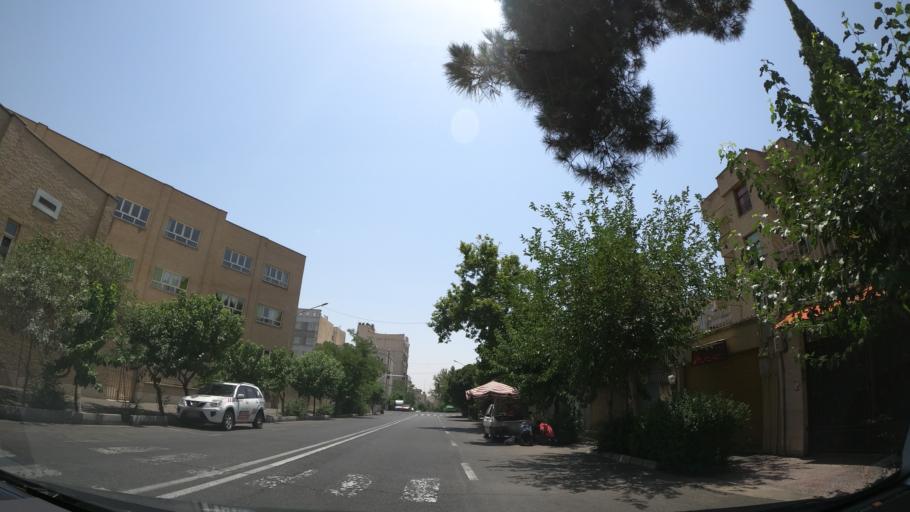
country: IR
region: Tehran
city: Tehran
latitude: 35.7208
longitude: 51.4262
